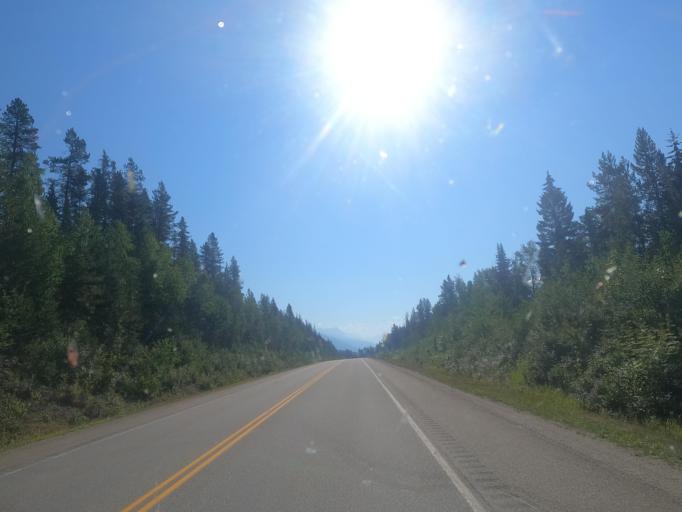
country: CA
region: Alberta
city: Jasper Park Lodge
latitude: 52.9763
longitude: -118.9639
